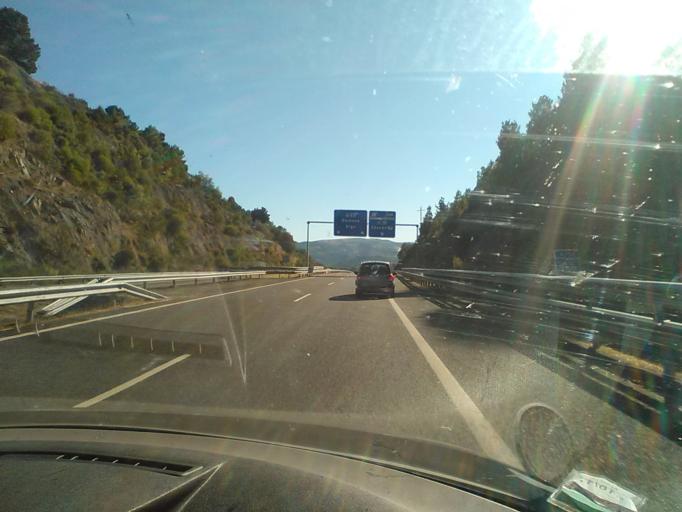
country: ES
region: Galicia
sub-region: Provincia de Ourense
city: Verin
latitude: 41.9151
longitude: -7.4234
